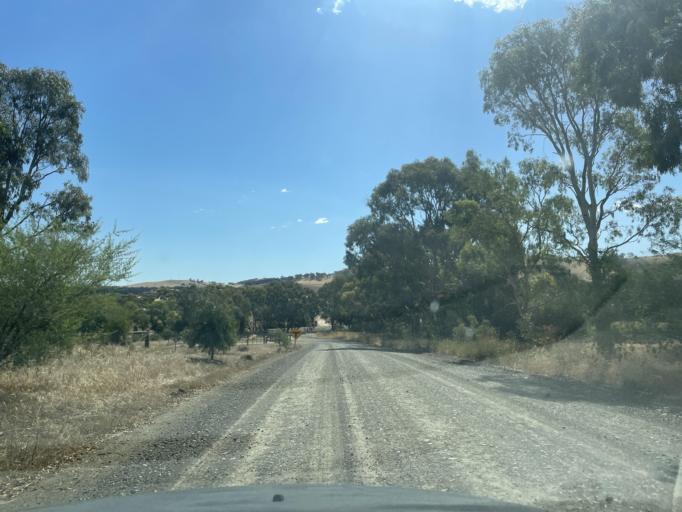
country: AU
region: South Australia
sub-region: Clare and Gilbert Valleys
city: Clare
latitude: -33.9123
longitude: 138.7185
